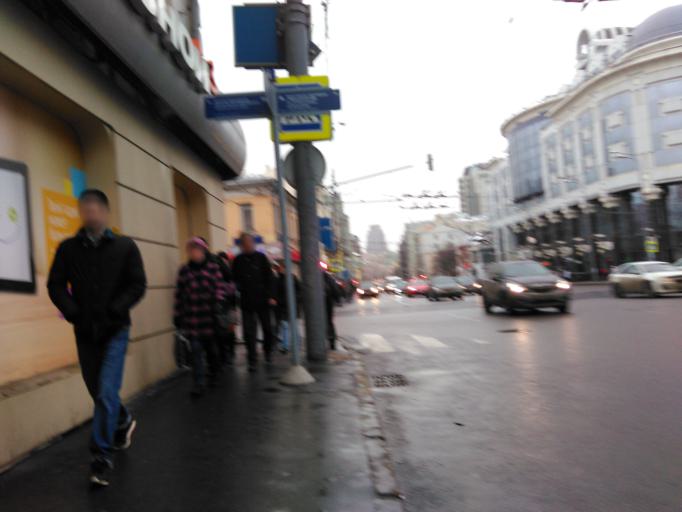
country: RU
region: Moscow
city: Mar'ina Roshcha
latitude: 55.7843
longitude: 37.5968
